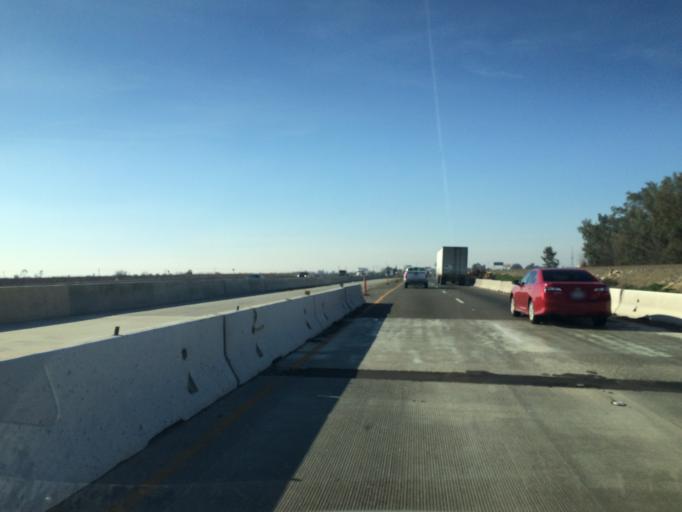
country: US
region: California
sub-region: Fresno County
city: Kingsburg
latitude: 36.4972
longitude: -119.5316
